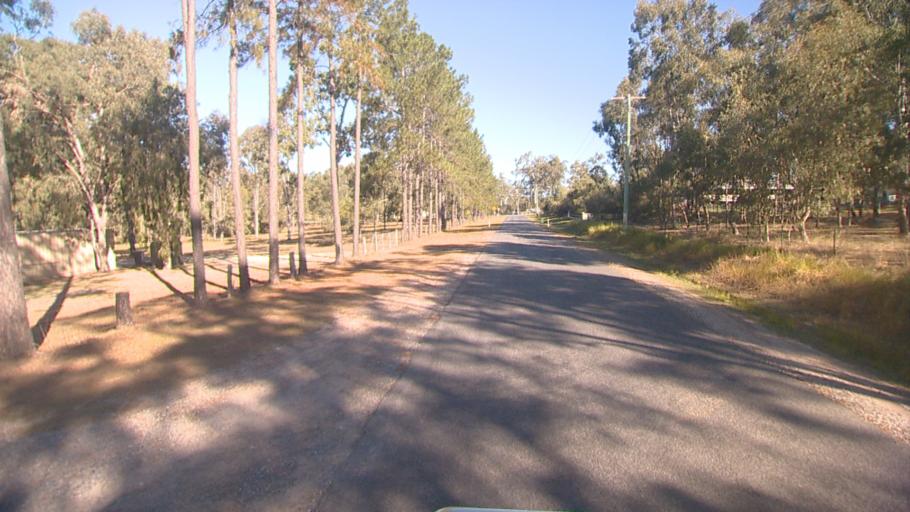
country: AU
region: Queensland
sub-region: Logan
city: Park Ridge South
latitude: -27.7346
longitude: 153.0217
